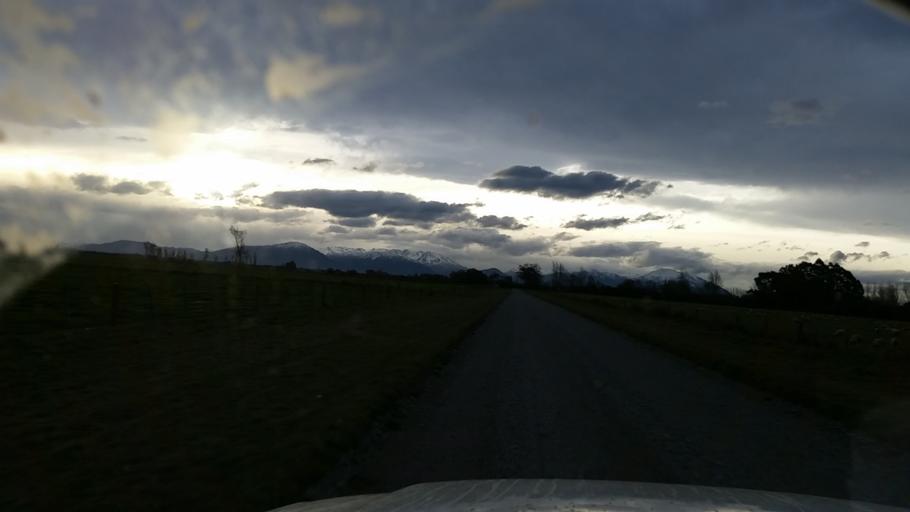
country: NZ
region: Canterbury
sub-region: Ashburton District
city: Ashburton
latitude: -43.8418
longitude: 171.6579
